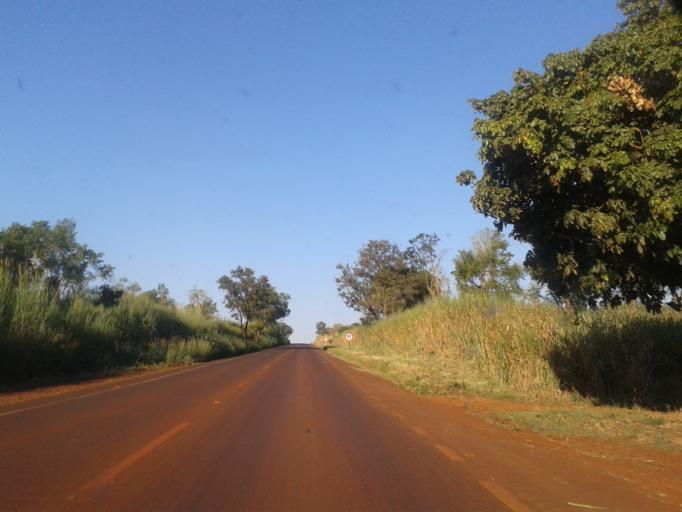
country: BR
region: Minas Gerais
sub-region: Capinopolis
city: Capinopolis
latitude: -18.7014
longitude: -49.6608
